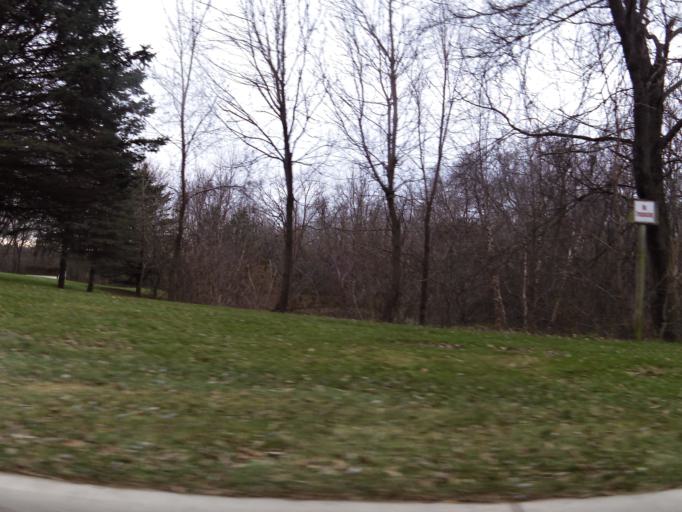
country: US
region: Minnesota
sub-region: Washington County
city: Lake Elmo
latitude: 44.9830
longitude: -92.8784
